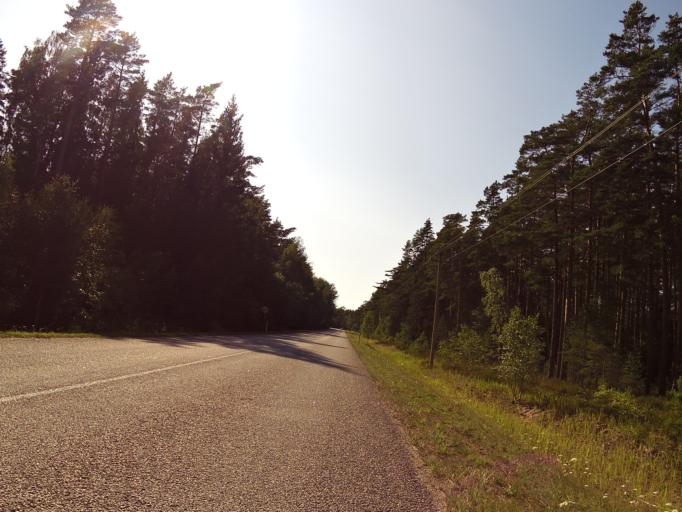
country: EE
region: Hiiumaa
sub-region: Kaerdla linn
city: Kardla
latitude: 58.9131
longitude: 22.3333
